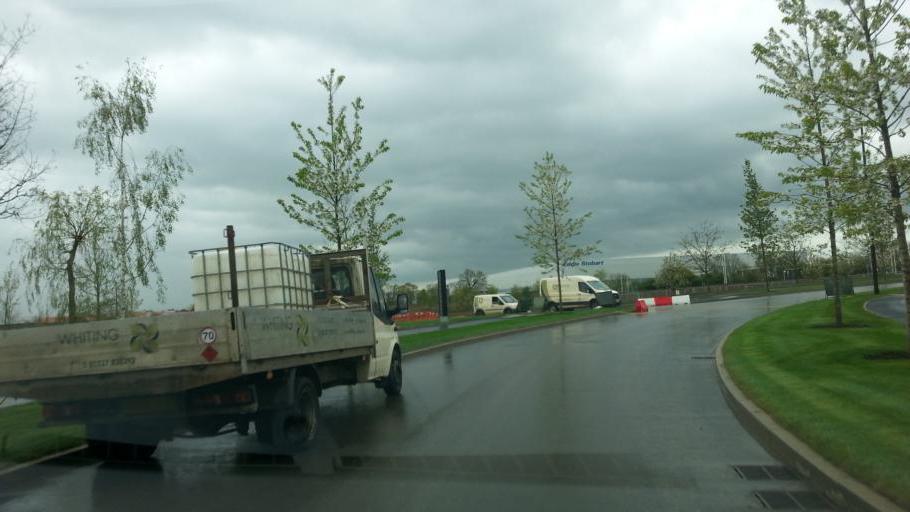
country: GB
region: England
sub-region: Warwickshire
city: Rugby
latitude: 52.3567
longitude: -1.1873
